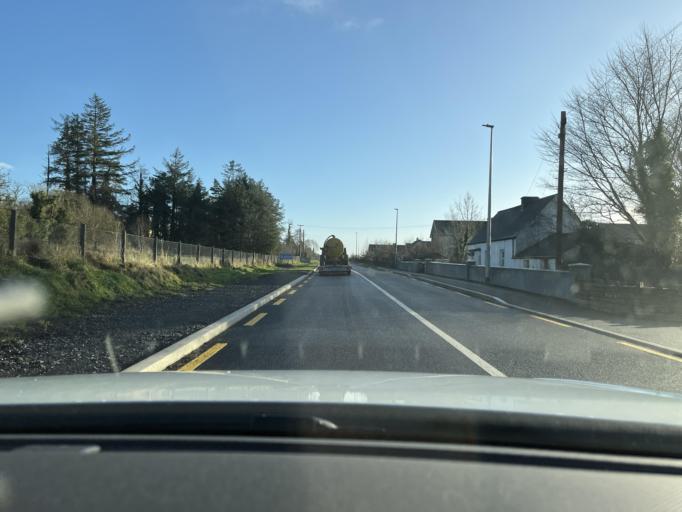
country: IE
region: Connaught
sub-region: County Leitrim
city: Manorhamilton
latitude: 54.1743
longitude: -8.1514
